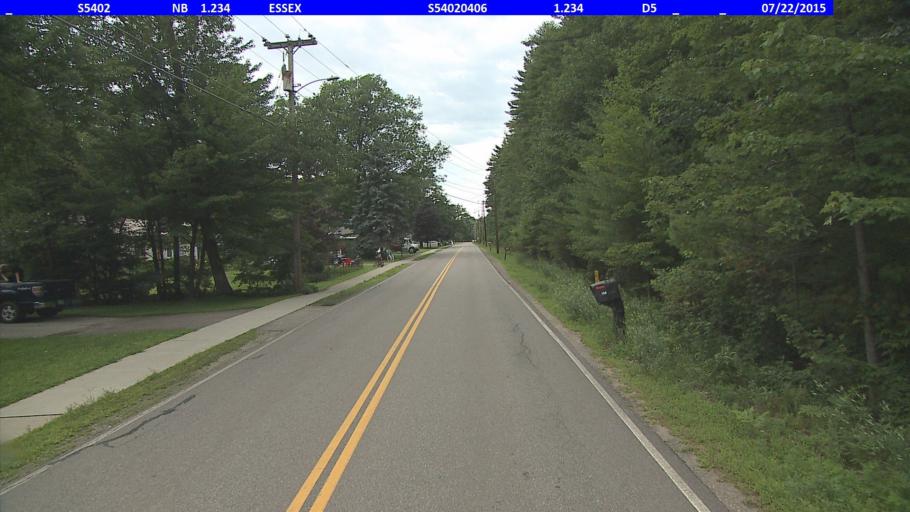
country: US
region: Vermont
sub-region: Chittenden County
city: Jericho
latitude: 44.4960
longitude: -73.0496
